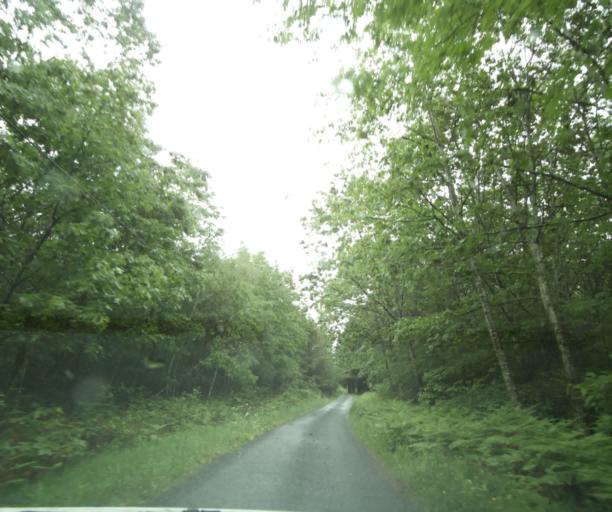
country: FR
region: Bourgogne
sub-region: Departement de Saone-et-Loire
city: Palinges
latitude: 46.5354
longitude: 4.2633
